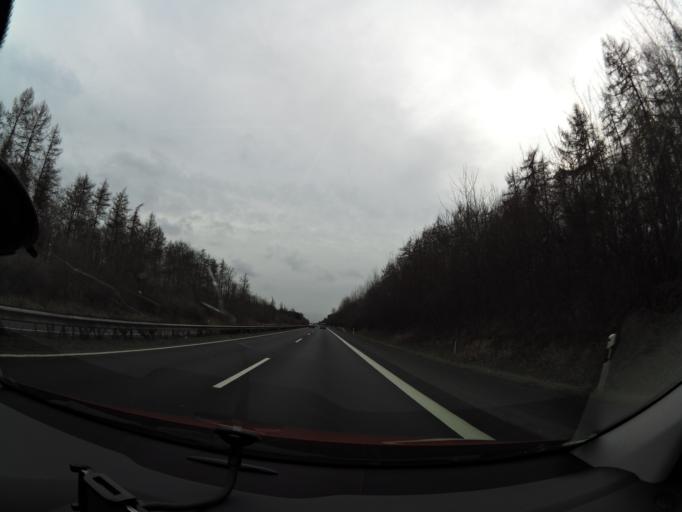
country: DE
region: Lower Saxony
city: Flothe
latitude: 52.1095
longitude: 10.4885
